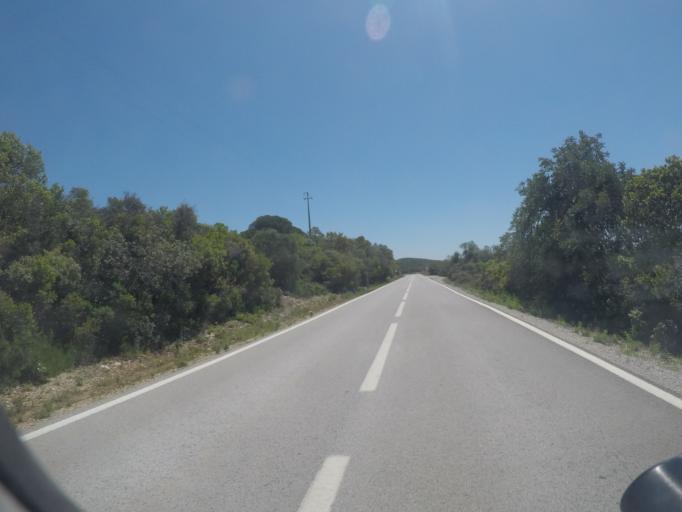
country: PT
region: Setubal
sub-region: Sesimbra
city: Sesimbra
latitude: 38.4625
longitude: -9.0260
